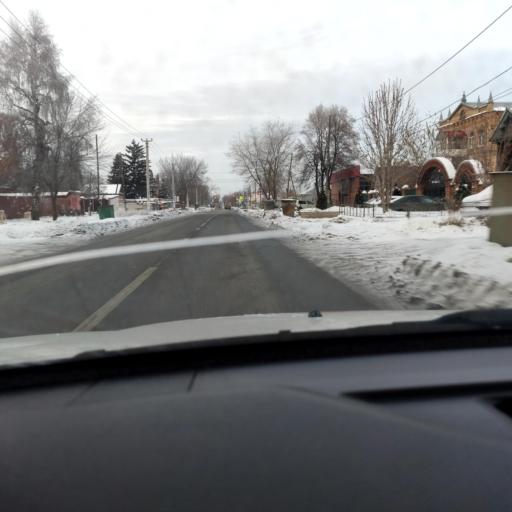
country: RU
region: Samara
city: Smyshlyayevka
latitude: 53.2498
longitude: 50.3382
